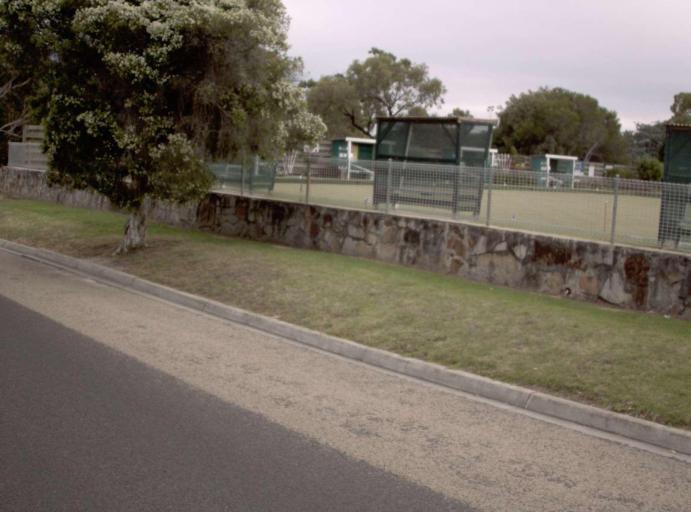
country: AU
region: Victoria
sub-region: East Gippsland
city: Bairnsdale
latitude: -37.9132
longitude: 147.7195
